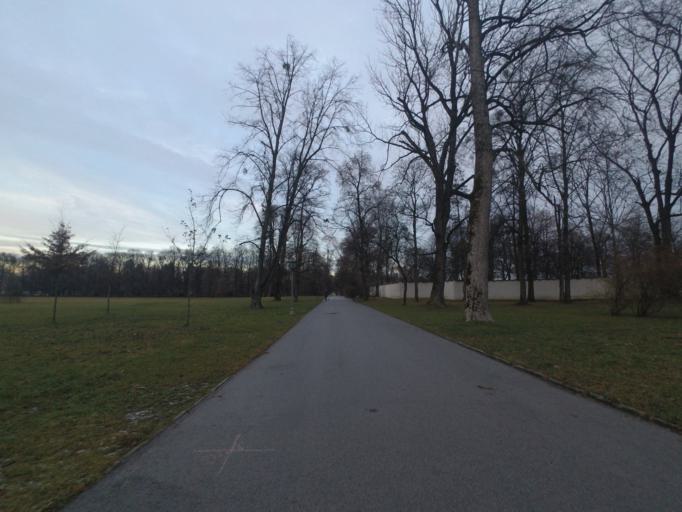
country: DE
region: Bavaria
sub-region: Upper Bavaria
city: Freilassing
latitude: 47.8169
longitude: 12.9942
